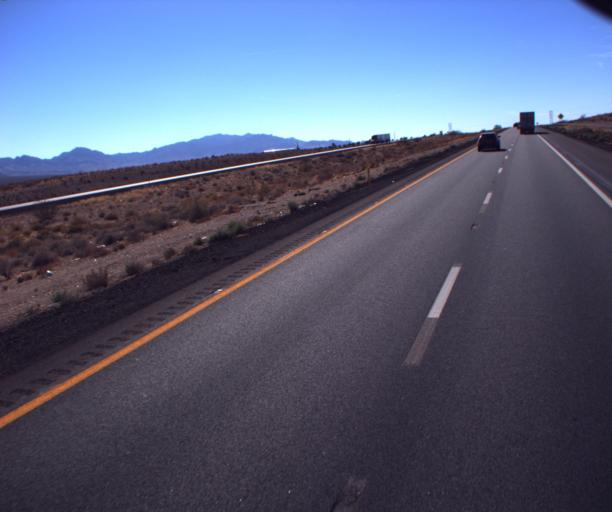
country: US
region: Arizona
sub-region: Mohave County
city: Beaver Dam
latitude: 36.8910
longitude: -113.9311
